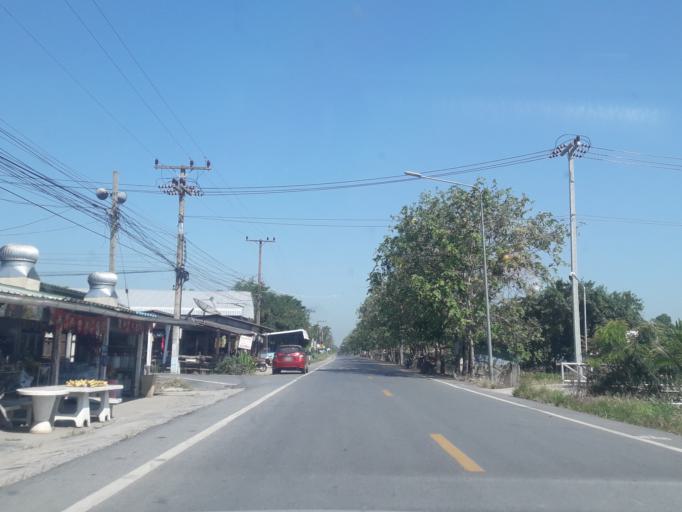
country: TH
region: Pathum Thani
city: Nong Suea
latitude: 14.1651
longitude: 100.8459
